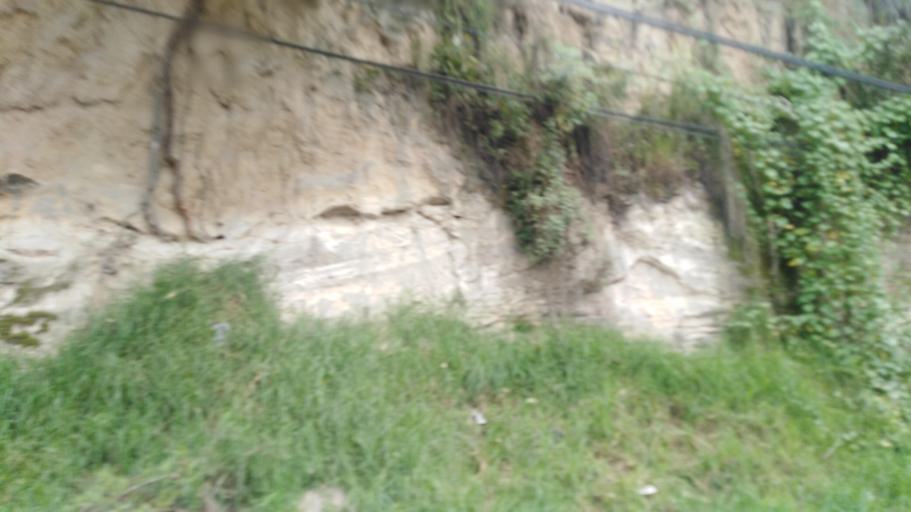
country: GT
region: Quetzaltenango
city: Quetzaltenango
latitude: 14.8529
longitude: -91.5124
